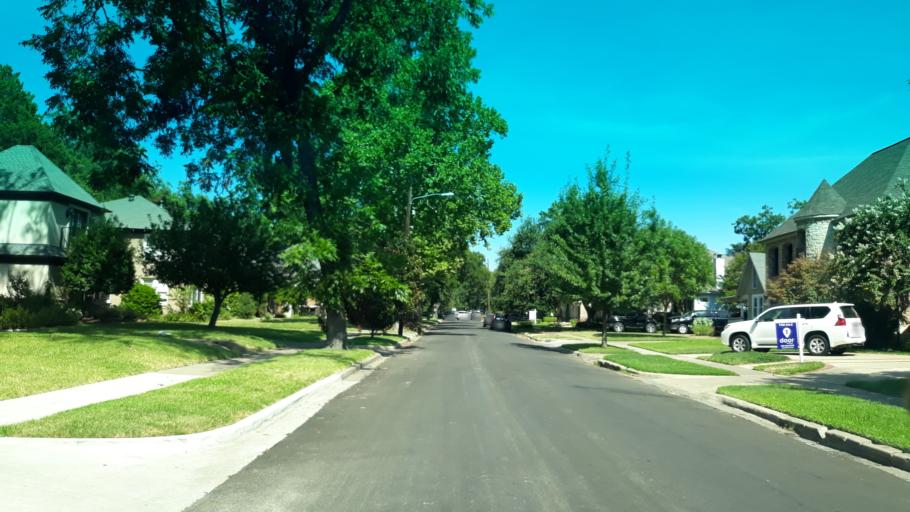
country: US
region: Texas
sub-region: Dallas County
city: Highland Park
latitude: 32.8182
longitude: -96.7611
